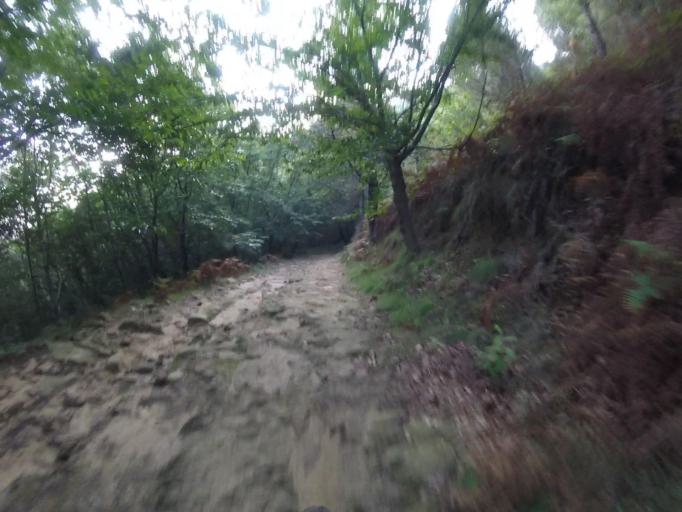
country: ES
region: Basque Country
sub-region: Provincia de Guipuzcoa
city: Fuenterrabia
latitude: 43.3460
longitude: -1.8445
